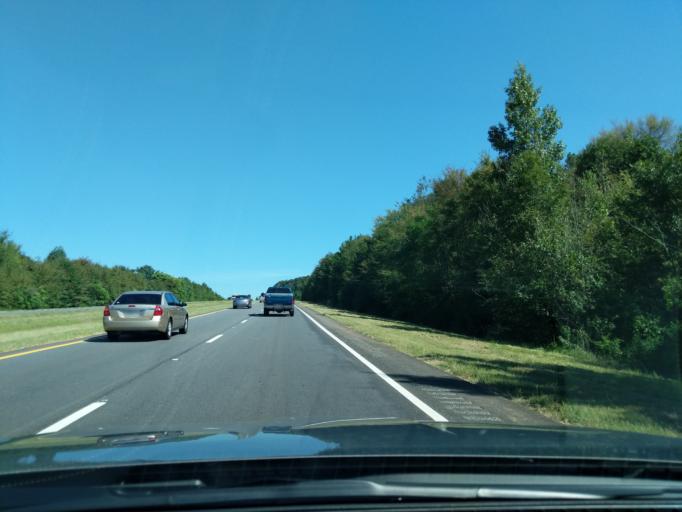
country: US
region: Georgia
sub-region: Jackson County
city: Commerce
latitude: 34.2270
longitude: -83.4500
